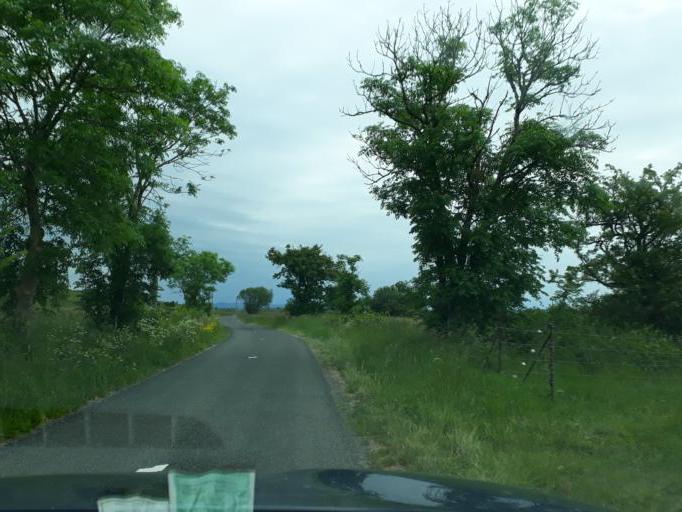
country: FR
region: Languedoc-Roussillon
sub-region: Departement de l'Herault
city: Lodeve
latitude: 43.8257
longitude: 3.2649
